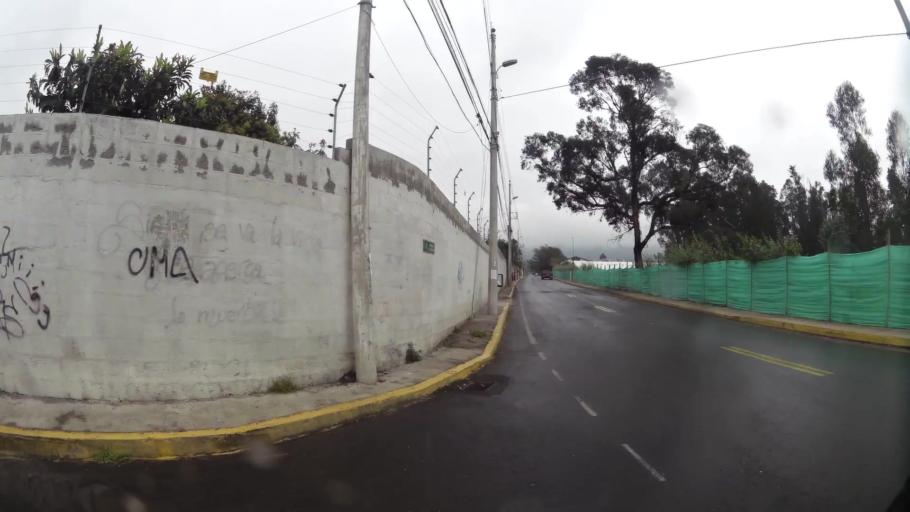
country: EC
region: Pichincha
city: Sangolqui
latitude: -0.2711
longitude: -78.4570
